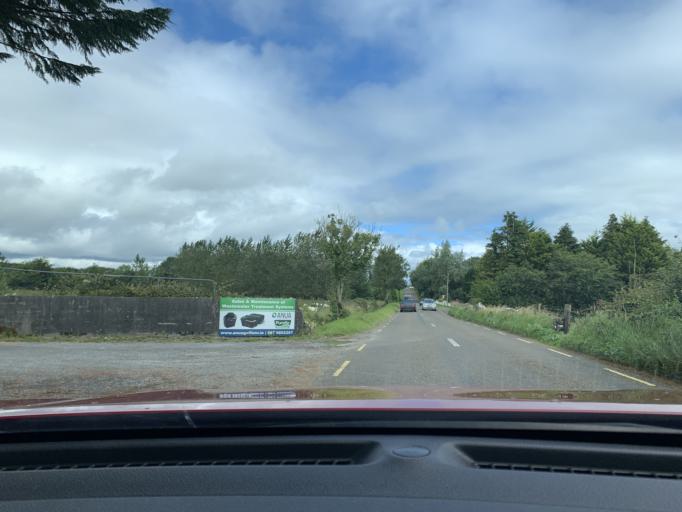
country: IE
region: Connaught
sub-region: County Leitrim
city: Carrick-on-Shannon
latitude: 53.9194
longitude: -8.1219
